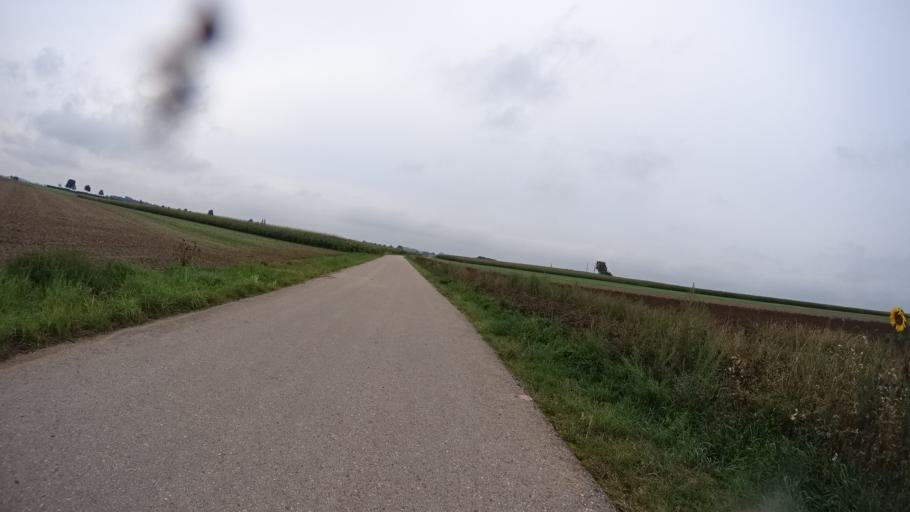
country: DE
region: Bavaria
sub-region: Upper Bavaria
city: Gaimersheim
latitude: 48.8241
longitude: 11.3625
